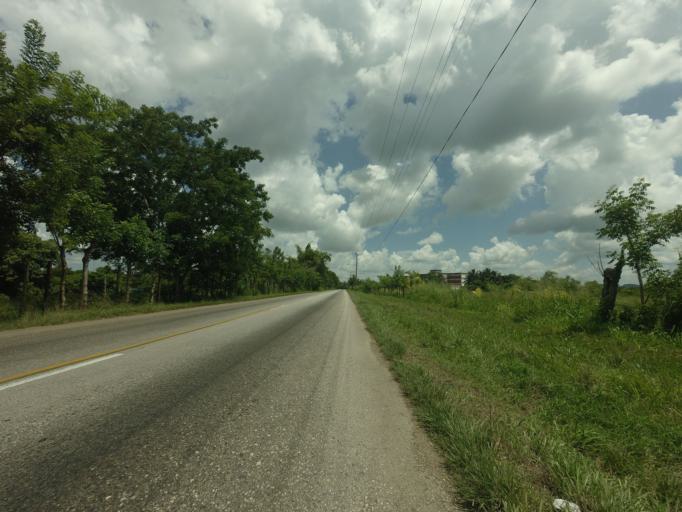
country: CU
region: La Habana
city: Arroyo Naranjo
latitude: 23.0187
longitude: -82.3080
